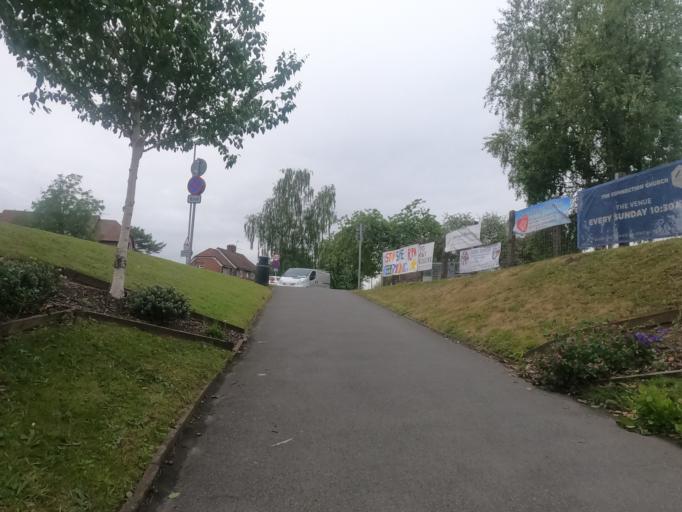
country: GB
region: England
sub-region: Cheshire West and Chester
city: Marston
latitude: 53.2501
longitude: -2.4834
